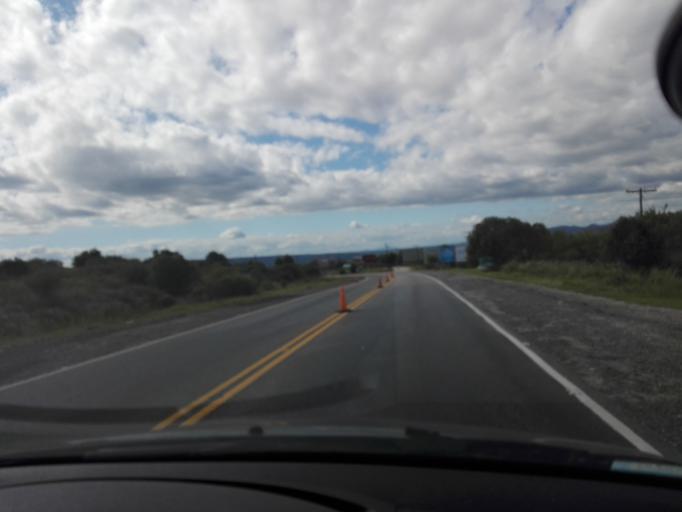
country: AR
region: Cordoba
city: Mina Clavero
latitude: -31.7508
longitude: -64.9779
